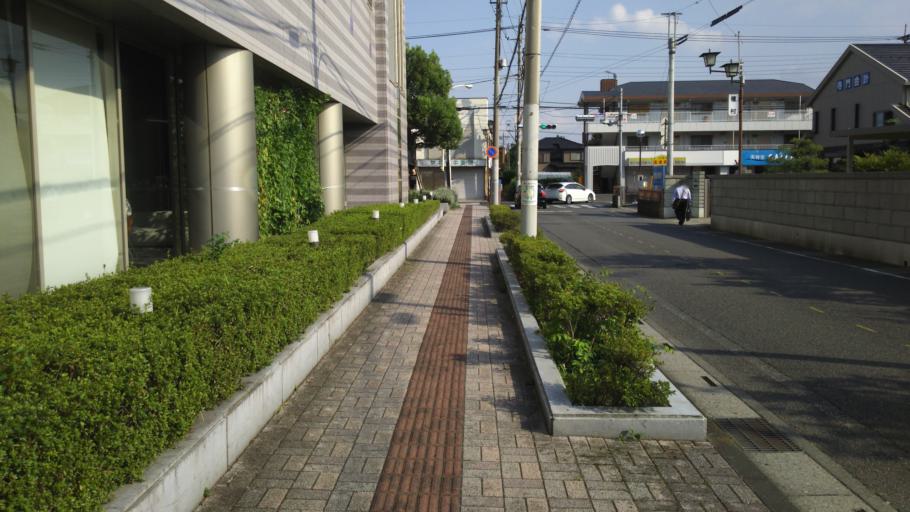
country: JP
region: Saitama
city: Kasukabe
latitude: 35.9773
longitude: 139.7426
